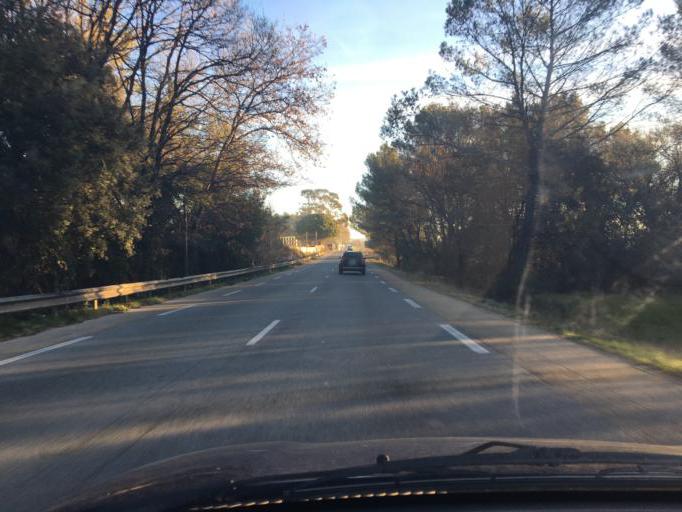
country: FR
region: Provence-Alpes-Cote d'Azur
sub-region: Departement du Var
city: La Motte
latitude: 43.4611
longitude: 6.5269
